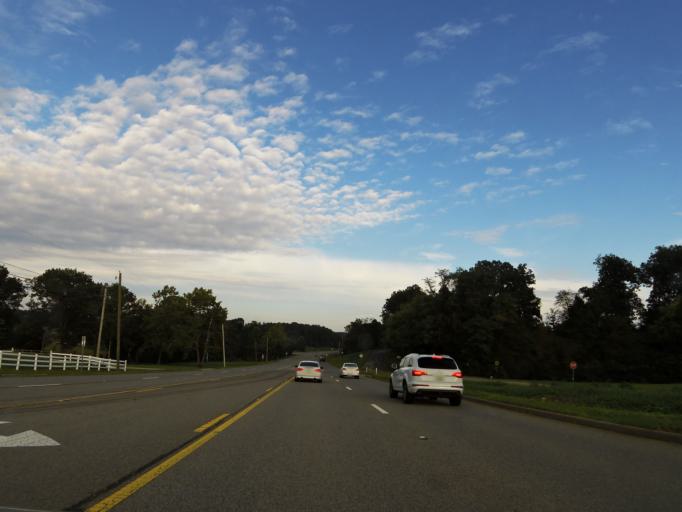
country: US
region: Alabama
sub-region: Lauderdale County
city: Rogersville
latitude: 34.8111
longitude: -87.2441
